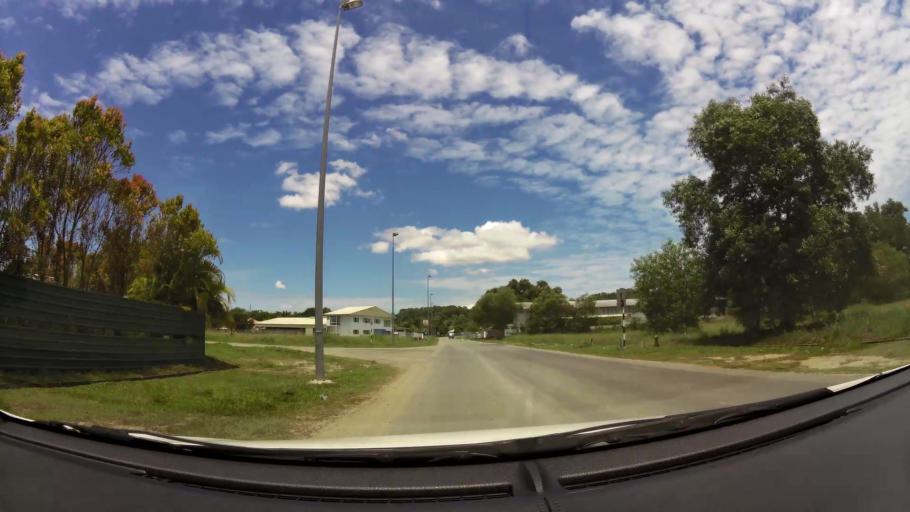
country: BN
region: Brunei and Muara
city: Bandar Seri Begawan
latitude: 4.9965
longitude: 115.0262
